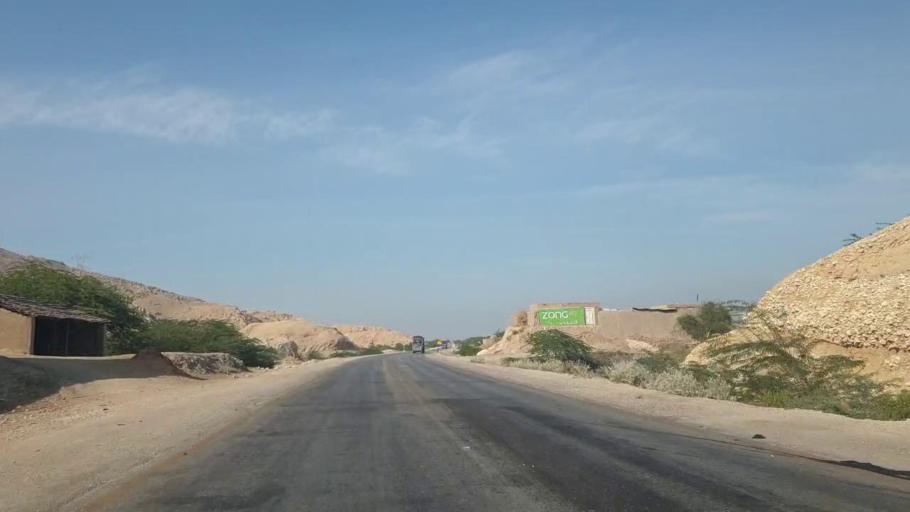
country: PK
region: Sindh
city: Sehwan
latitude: 26.3046
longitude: 67.8935
